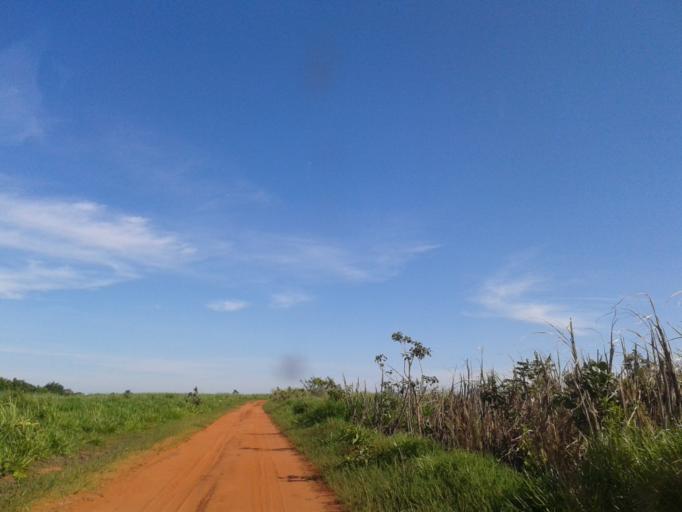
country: BR
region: Minas Gerais
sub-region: Santa Vitoria
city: Santa Vitoria
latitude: -19.1053
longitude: -49.9905
